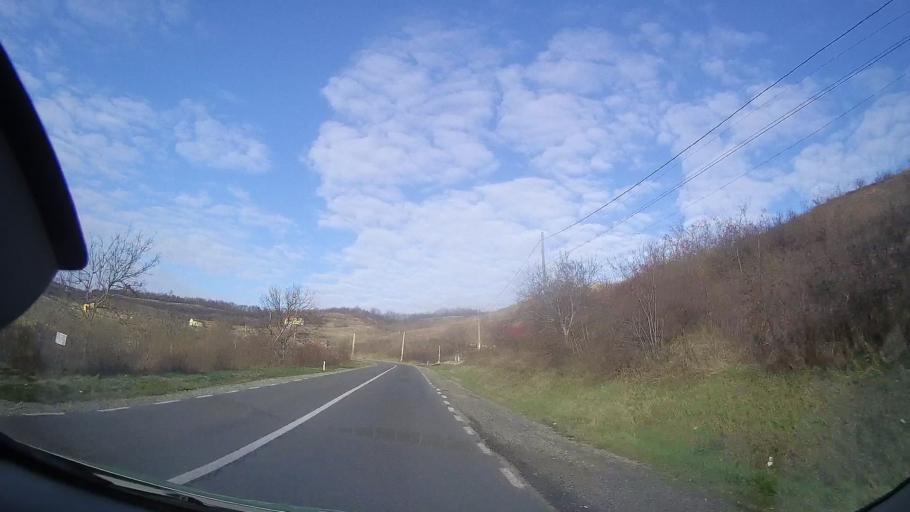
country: RO
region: Cluj
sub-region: Comuna Cojocna
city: Cojocna
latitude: 46.8062
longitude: 23.8405
